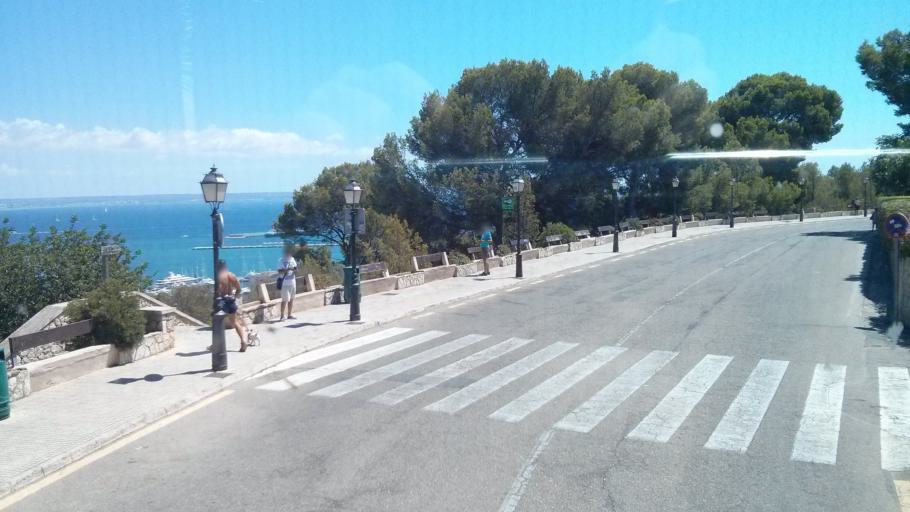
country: ES
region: Balearic Islands
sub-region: Illes Balears
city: Palma
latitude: 39.5644
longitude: 2.6198
